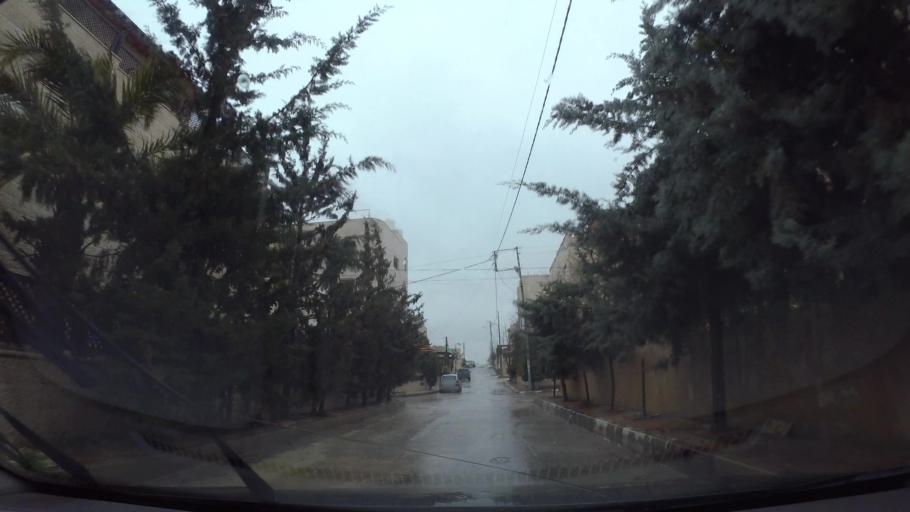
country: JO
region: Amman
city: Al Jubayhah
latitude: 32.0124
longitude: 35.8908
